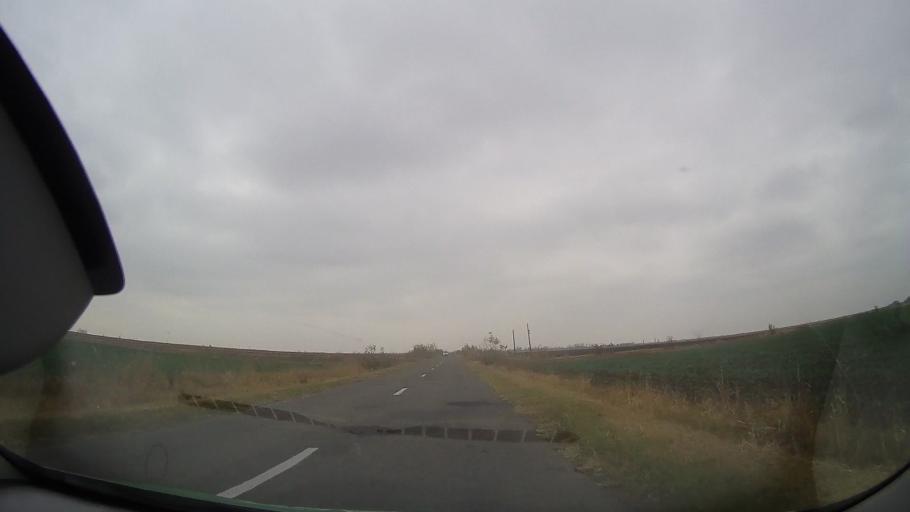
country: RO
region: Ialomita
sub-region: Comuna Valea Macrisului
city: Valea Macrisului
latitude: 44.7578
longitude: 26.8048
